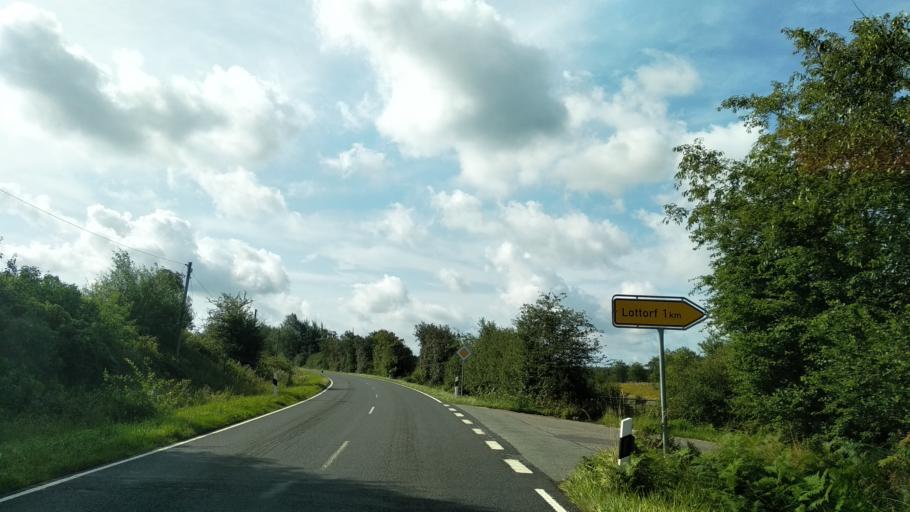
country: DE
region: Schleswig-Holstein
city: Lottorf
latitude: 54.4489
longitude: 9.5930
